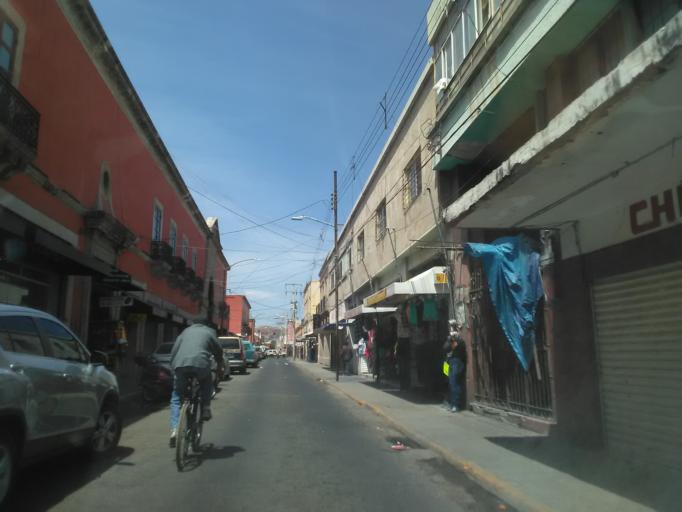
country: MX
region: Durango
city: Victoria de Durango
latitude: 24.0242
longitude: -104.6664
